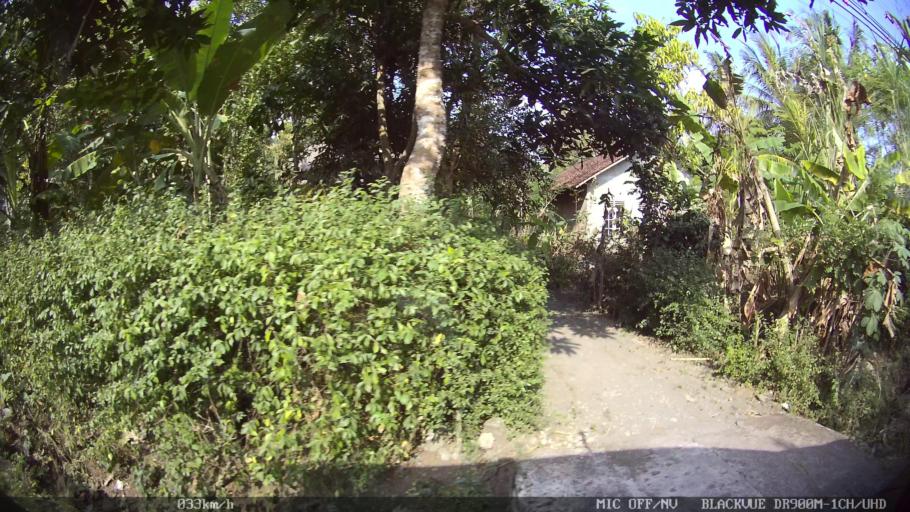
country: ID
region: Daerah Istimewa Yogyakarta
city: Kasihan
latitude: -7.8329
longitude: 110.3234
